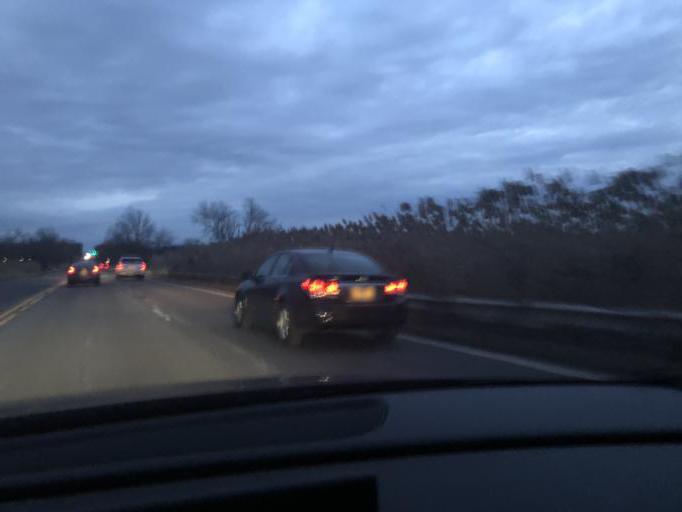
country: US
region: New Jersey
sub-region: Morris County
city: Madison
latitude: 40.7915
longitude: -74.4205
